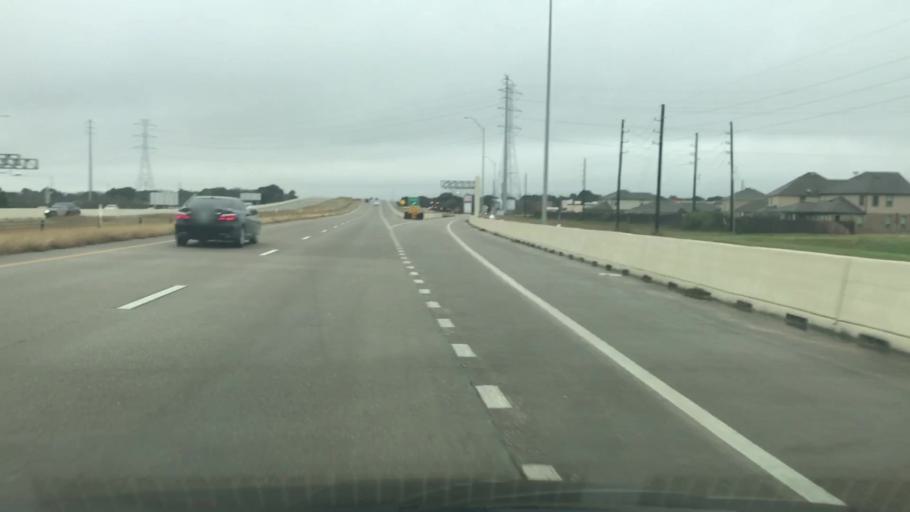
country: US
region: Texas
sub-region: Harris County
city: Katy
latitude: 29.8275
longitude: -95.7635
